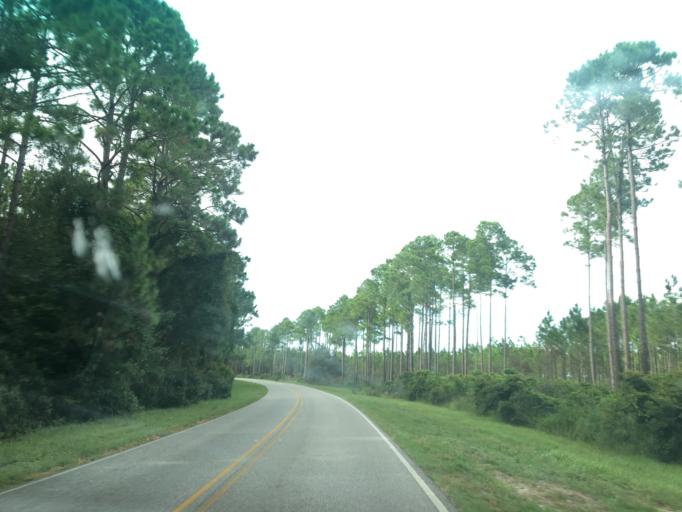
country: US
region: Florida
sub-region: Wakulla County
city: Crawfordville
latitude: 29.9334
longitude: -84.3784
